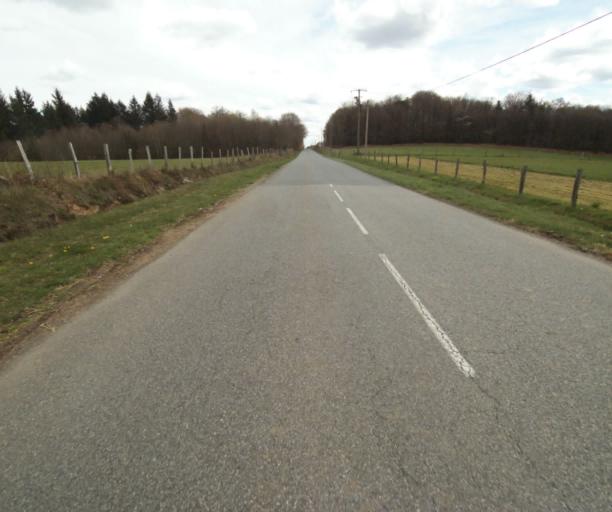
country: FR
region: Limousin
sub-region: Departement de la Correze
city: Laguenne
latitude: 45.2061
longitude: 1.8850
